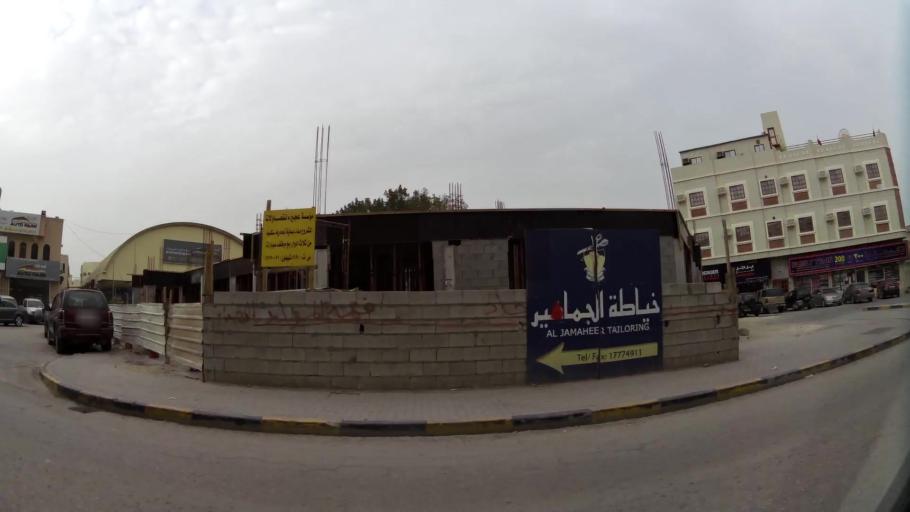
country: BH
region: Northern
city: Ar Rifa'
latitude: 26.1165
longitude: 50.5719
